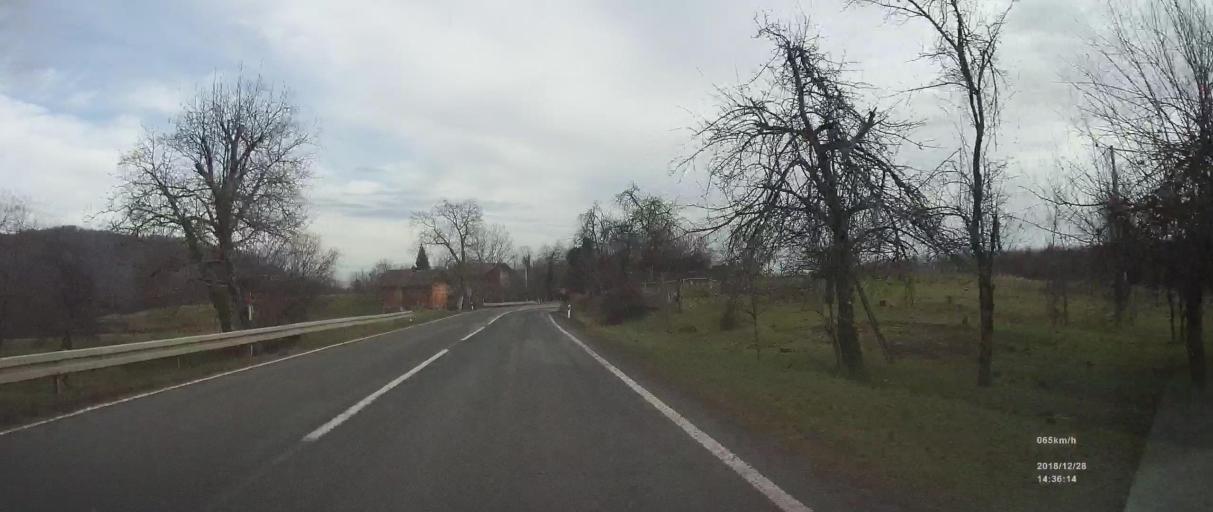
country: HR
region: Primorsko-Goranska
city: Vrbovsko
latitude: 45.4233
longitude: 15.1938
